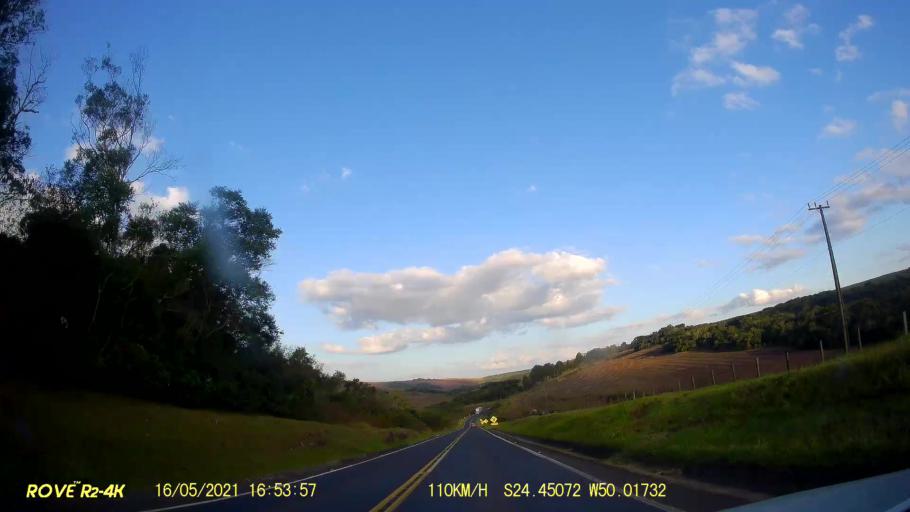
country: BR
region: Parana
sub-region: Pirai Do Sul
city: Pirai do Sul
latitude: -24.4507
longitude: -50.0170
